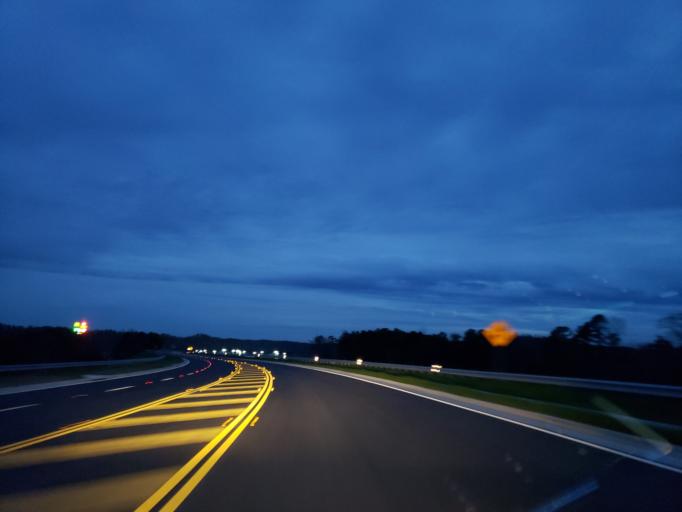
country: US
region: Georgia
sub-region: Bartow County
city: Emerson
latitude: 34.1254
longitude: -84.7421
